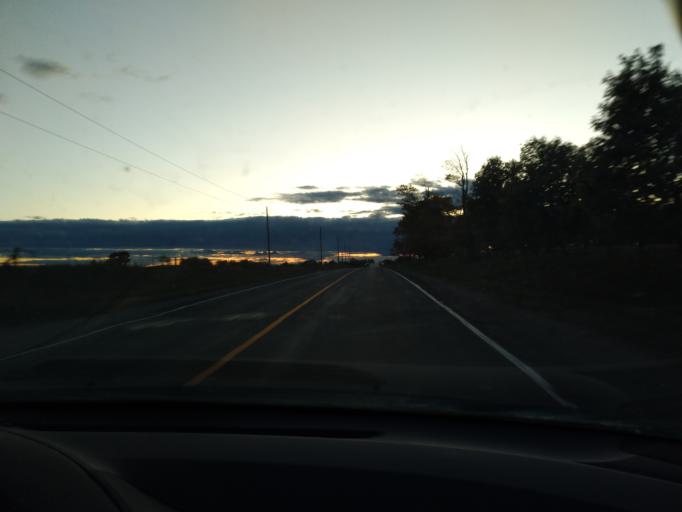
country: CA
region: Ontario
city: Innisfil
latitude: 44.2383
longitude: -79.6604
